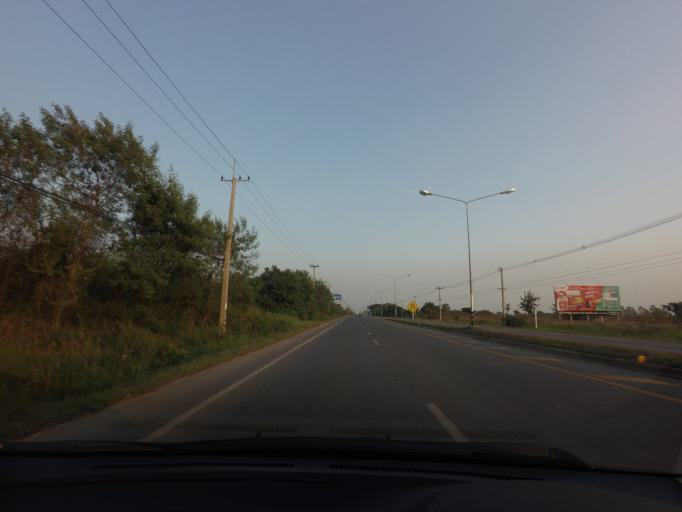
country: TH
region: Sukhothai
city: Sukhothai
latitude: 17.0247
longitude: 99.8909
